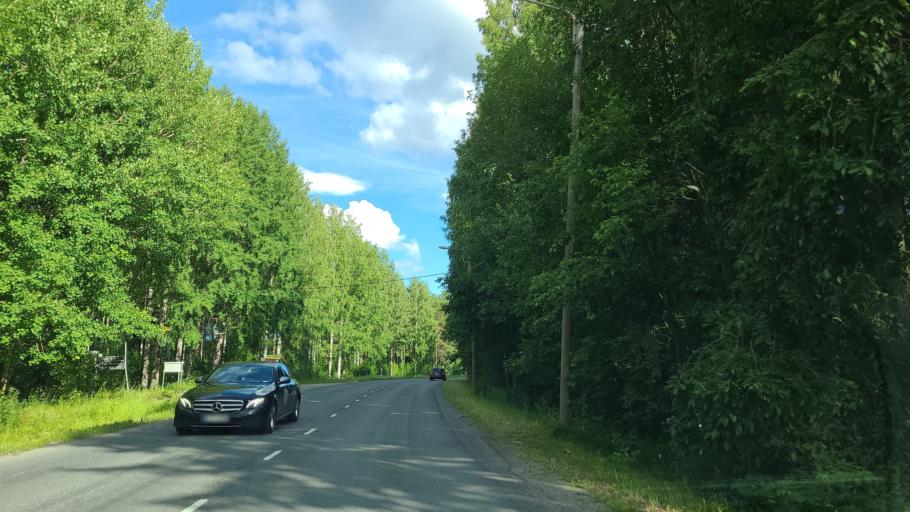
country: FI
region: Northern Savo
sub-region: Kuopio
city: Kuopio
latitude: 62.9357
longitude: 27.6623
